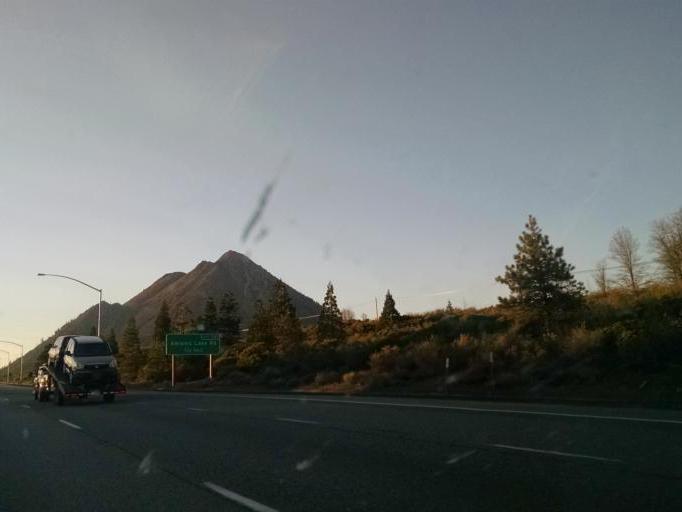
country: US
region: California
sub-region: Siskiyou County
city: Mount Shasta
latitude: 41.3336
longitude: -122.3334
